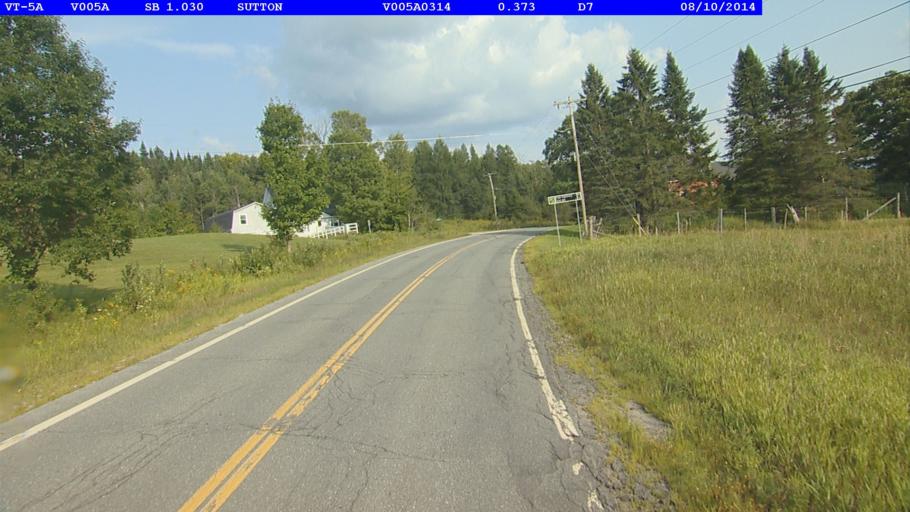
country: US
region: Vermont
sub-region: Caledonia County
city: Lyndonville
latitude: 44.6552
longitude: -71.9833
